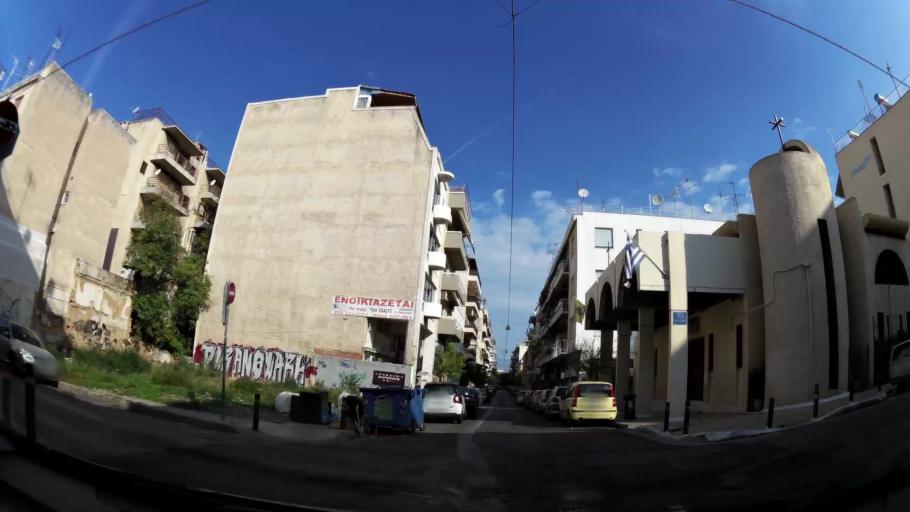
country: GR
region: Attica
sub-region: Nomarchia Athinas
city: Nea Chalkidona
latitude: 38.0169
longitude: 23.7364
